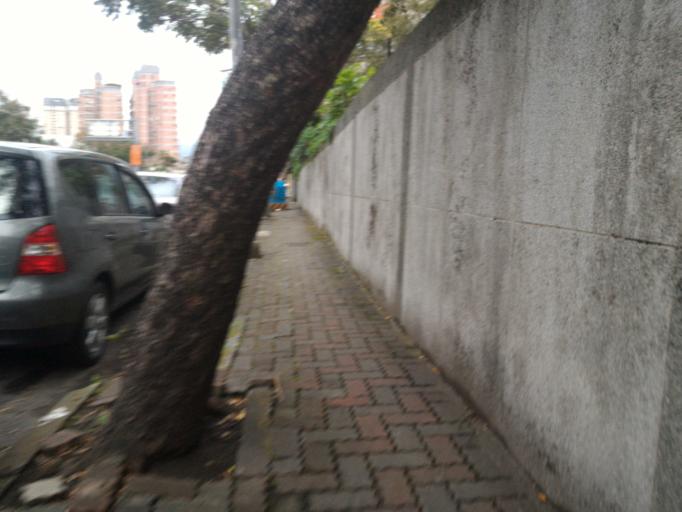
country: TW
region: Taipei
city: Taipei
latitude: 24.9874
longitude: 121.5358
